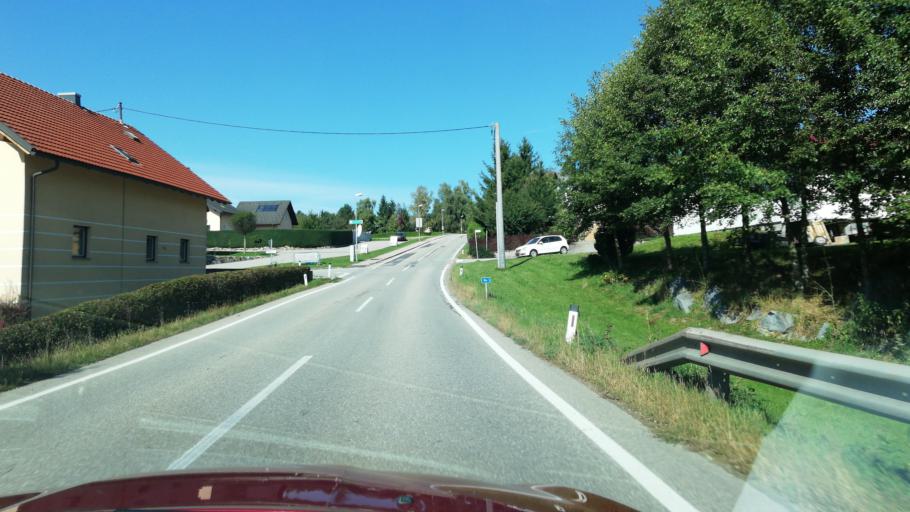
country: AT
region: Upper Austria
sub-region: Politischer Bezirk Vocklabruck
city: Zell am Pettenfirst
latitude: 48.1445
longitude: 13.5704
